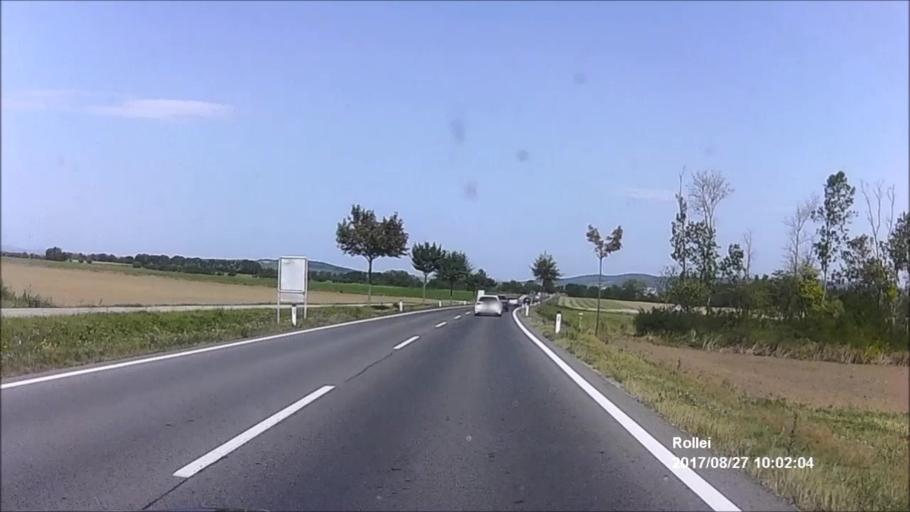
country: AT
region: Burgenland
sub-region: Eisenstadt-Umgebung
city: Zagersdorf
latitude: 47.7814
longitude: 16.5213
